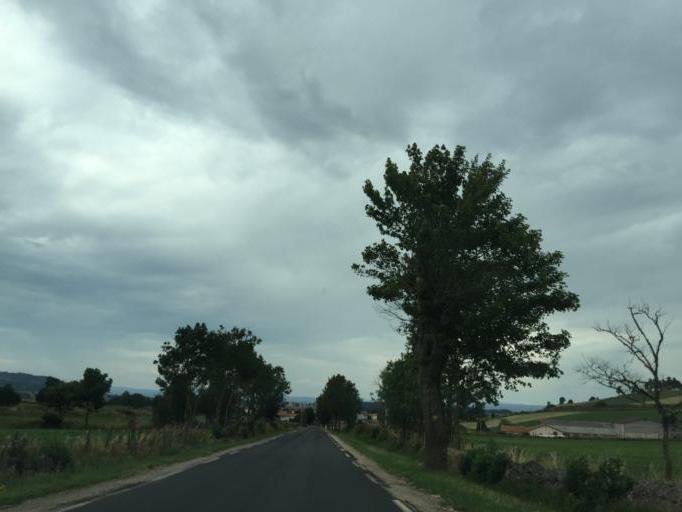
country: FR
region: Languedoc-Roussillon
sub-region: Departement de la Lozere
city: Langogne
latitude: 44.8500
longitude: 3.8385
